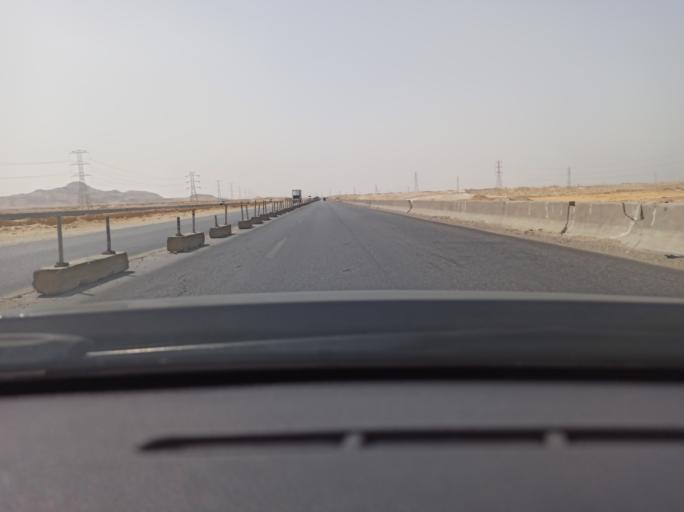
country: EG
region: Muhafazat Bani Suwayf
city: Bush
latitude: 29.1395
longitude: 31.2281
